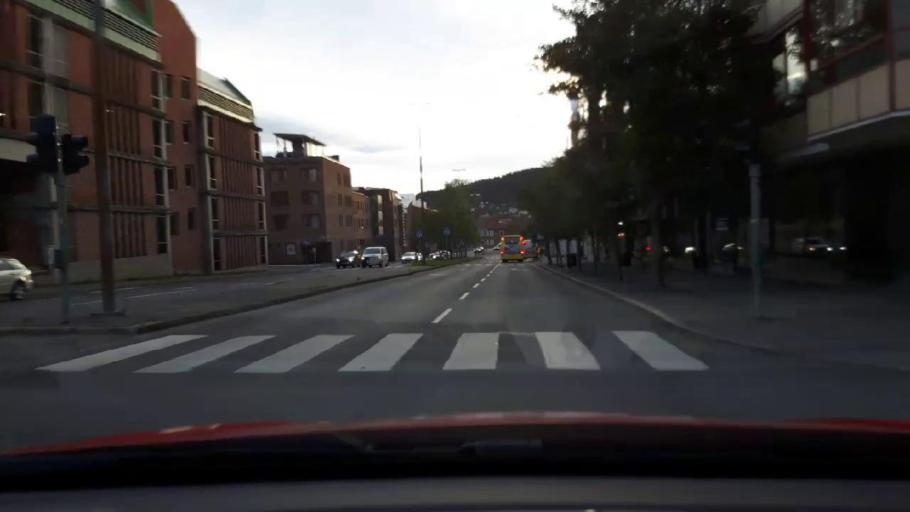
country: SE
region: Jaemtland
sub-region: OEstersunds Kommun
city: Ostersund
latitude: 63.1807
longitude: 14.6379
